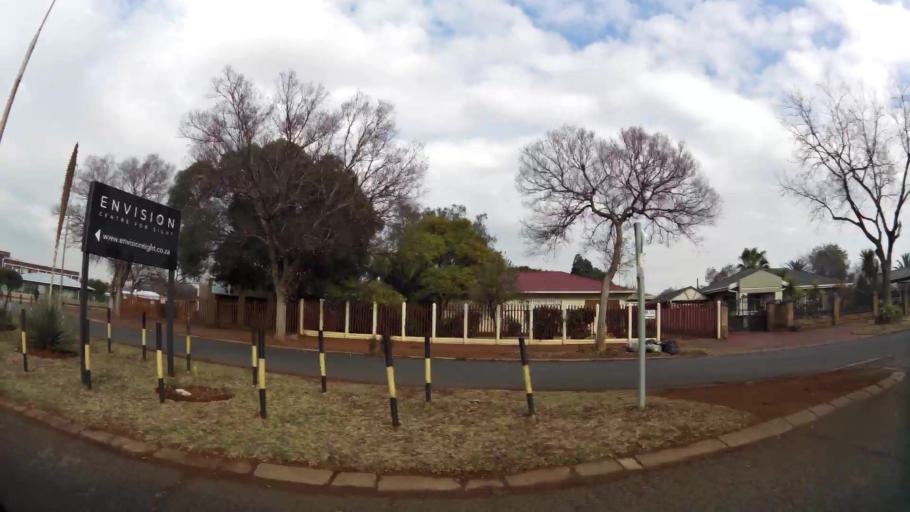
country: ZA
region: Gauteng
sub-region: Sedibeng District Municipality
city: Vanderbijlpark
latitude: -26.7014
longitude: 27.8314
